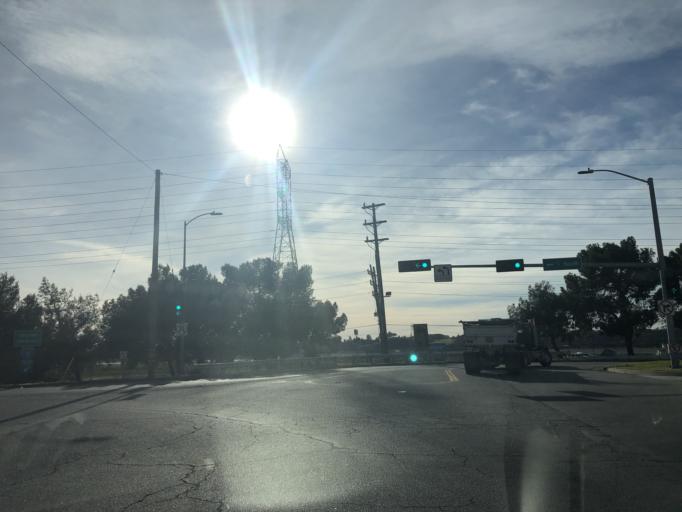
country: US
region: California
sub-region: Los Angeles County
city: San Fernando
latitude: 34.3035
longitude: -118.4785
